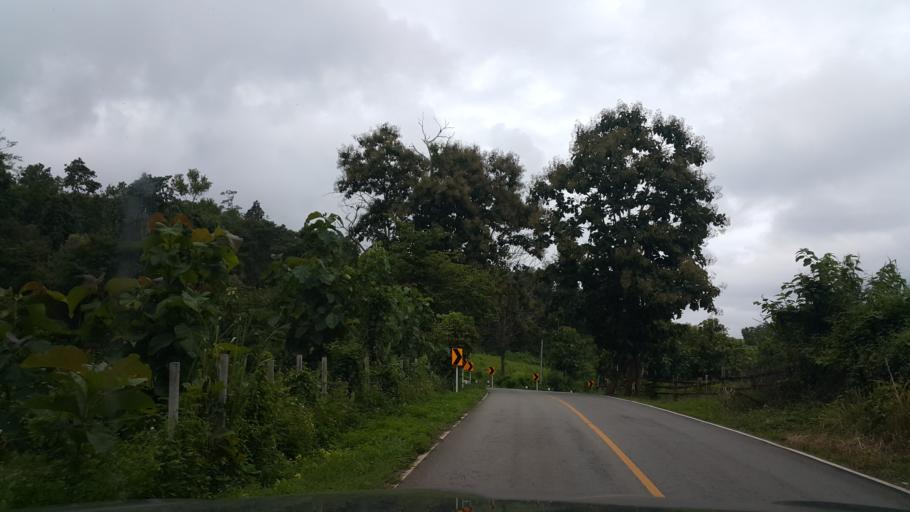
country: TH
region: Chiang Mai
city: Samoeng
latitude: 18.8610
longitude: 98.6450
